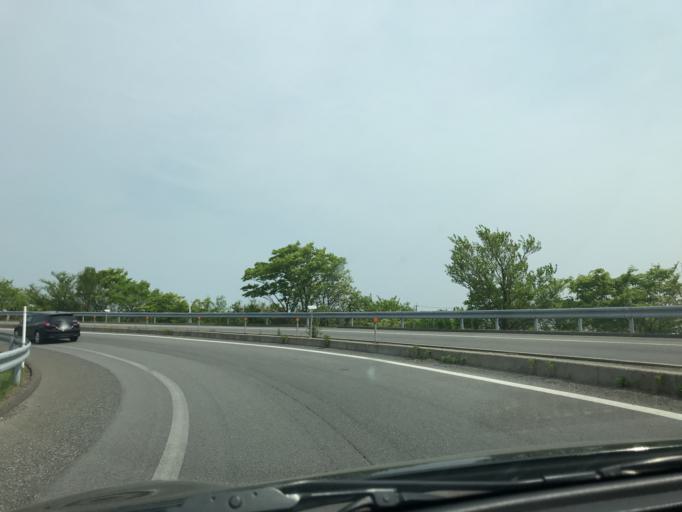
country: JP
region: Niigata
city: Kameda-honcho
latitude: 37.8790
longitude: 139.0835
